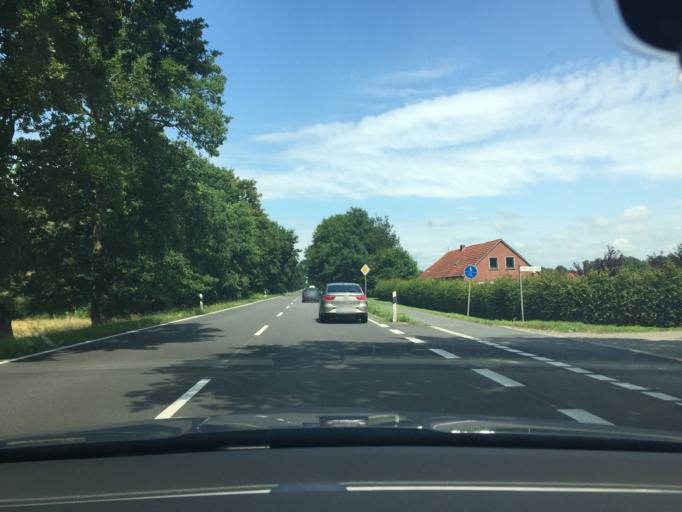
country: DE
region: Lower Saxony
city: Hesel
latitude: 53.3162
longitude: 7.5975
